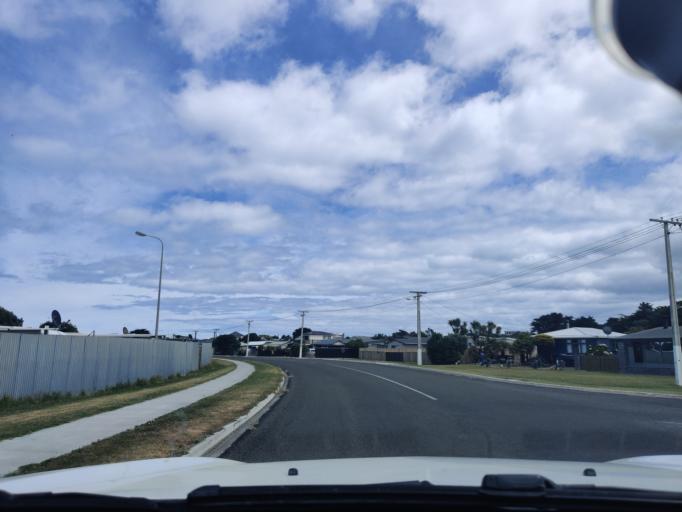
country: NZ
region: Manawatu-Wanganui
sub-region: Horowhenua District
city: Foxton
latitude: -40.4614
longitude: 175.2243
